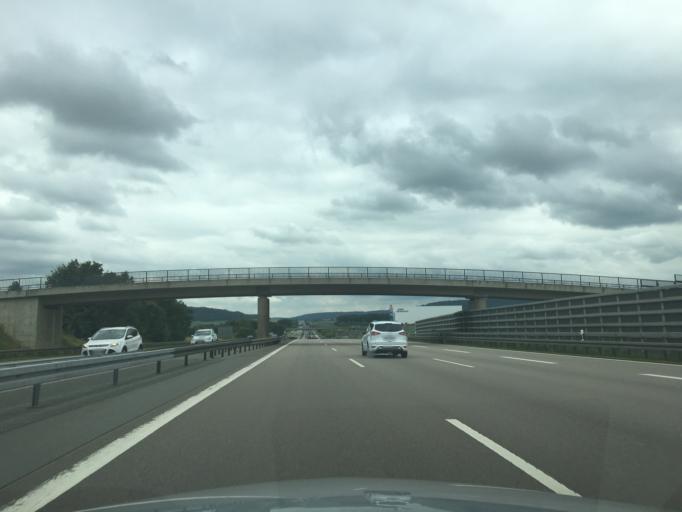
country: DE
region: Bavaria
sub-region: Upper Palatinate
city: Freystadt
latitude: 49.1687
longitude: 11.2623
